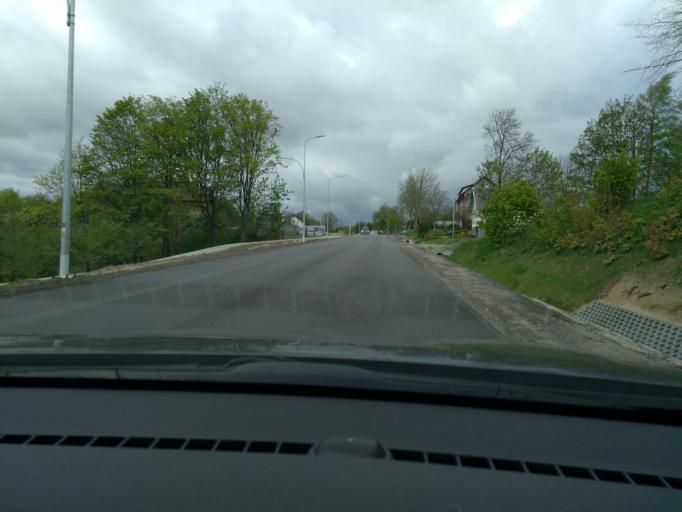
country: PL
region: Pomeranian Voivodeship
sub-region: Powiat kartuski
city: Sierakowice
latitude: 54.3413
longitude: 17.9675
